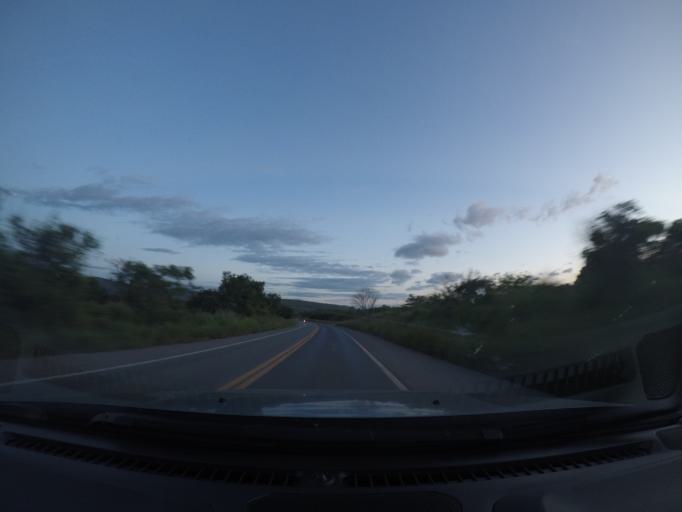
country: BR
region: Bahia
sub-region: Seabra
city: Seabra
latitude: -12.4824
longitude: -41.7381
